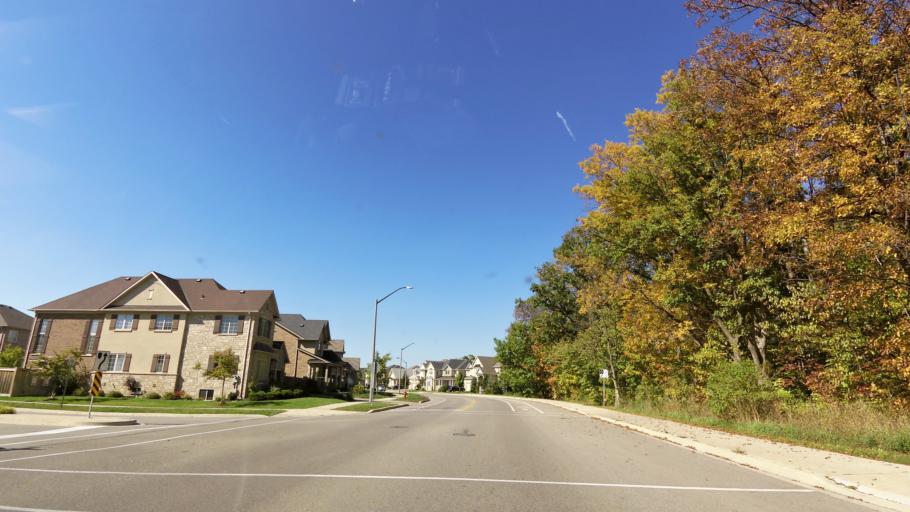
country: CA
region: Ontario
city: Burlington
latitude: 43.4264
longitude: -79.7781
